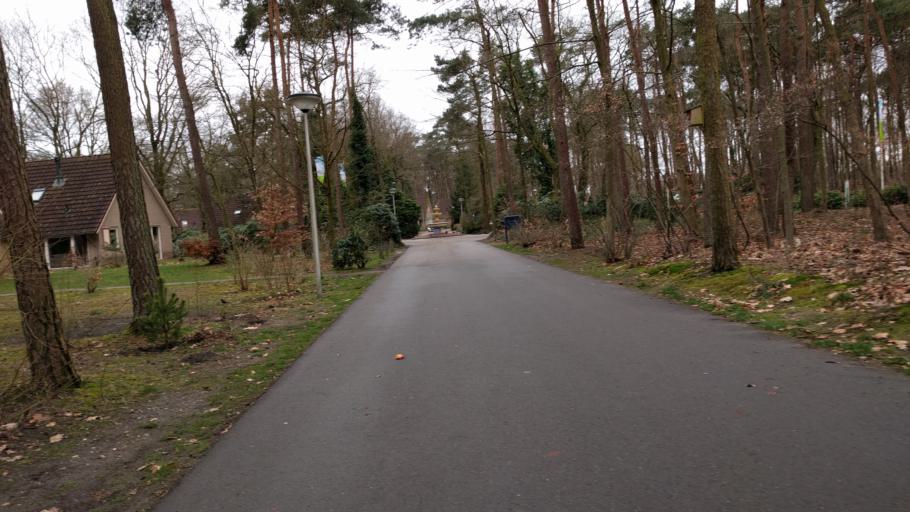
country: NL
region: Gelderland
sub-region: Gemeente Oldebroek
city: Oldebroek
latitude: 52.4420
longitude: 5.9544
